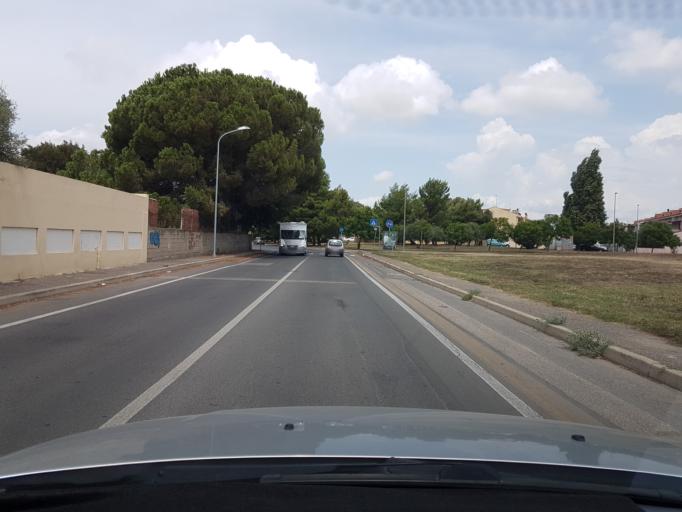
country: IT
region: Sardinia
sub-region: Provincia di Oristano
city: Oristano
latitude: 39.9124
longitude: 8.5901
